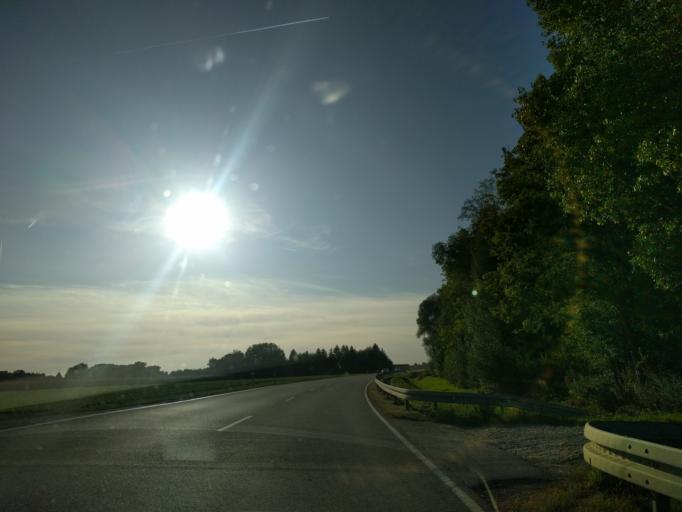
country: DE
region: Bavaria
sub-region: Lower Bavaria
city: Osterhofen
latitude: 48.7153
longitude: 13.0288
